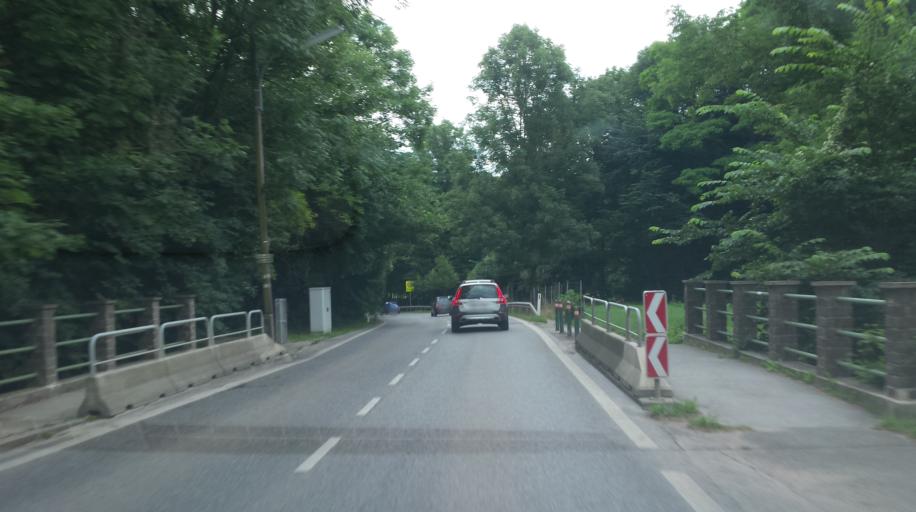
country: AT
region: Lower Austria
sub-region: Politischer Bezirk Wien-Umgebung
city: Purkersdorf
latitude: 48.2240
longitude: 16.2097
